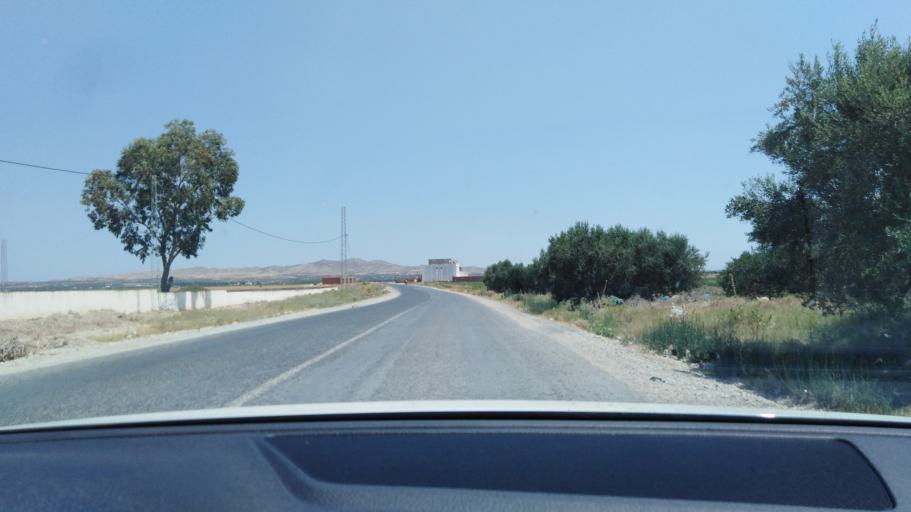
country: TN
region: Al Qayrawan
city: Sbikha
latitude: 36.1141
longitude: 10.0991
